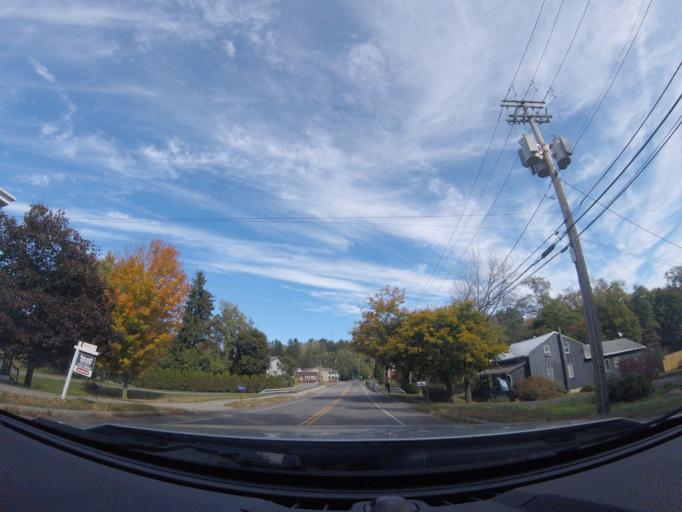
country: US
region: New York
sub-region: Tompkins County
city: Dryden
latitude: 42.5510
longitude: -76.2924
